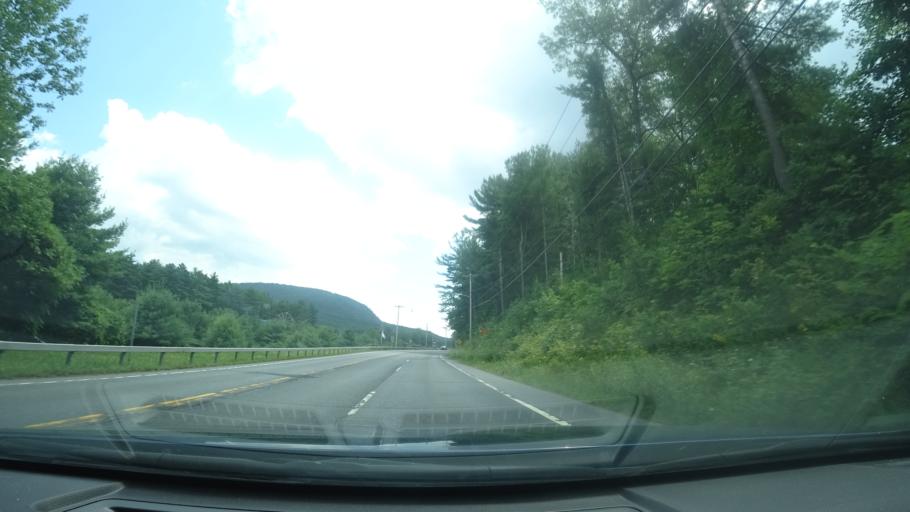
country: US
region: New York
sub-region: Warren County
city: Glens Falls North
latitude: 43.3976
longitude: -73.7048
